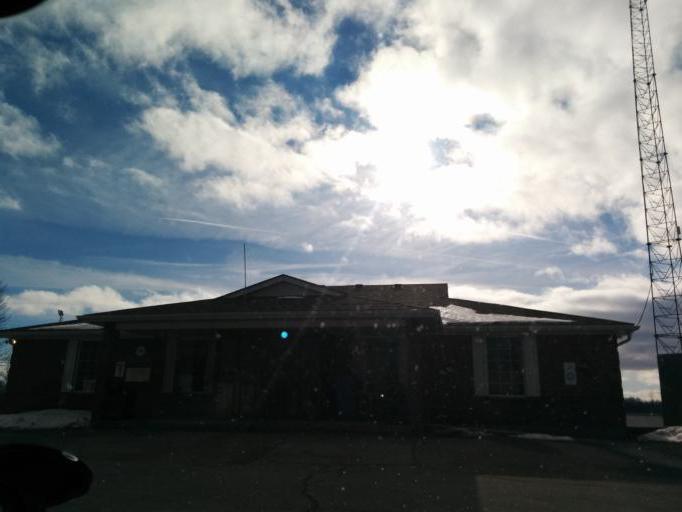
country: CA
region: Ontario
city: Brantford
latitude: 43.0003
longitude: -80.0951
